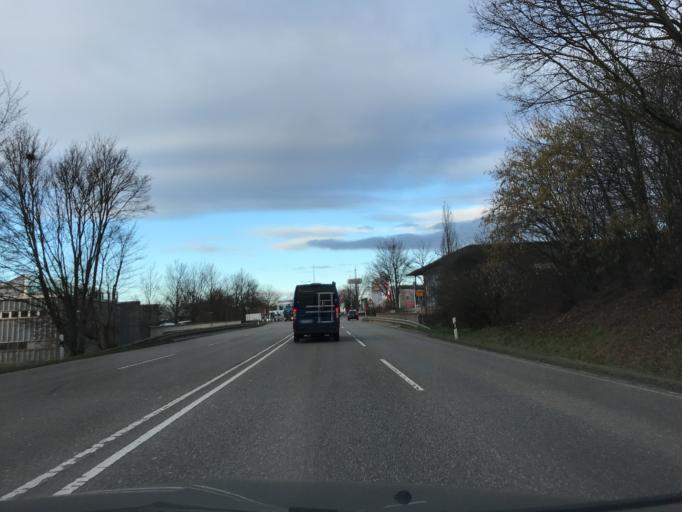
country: DE
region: Baden-Wuerttemberg
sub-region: Regierungsbezirk Stuttgart
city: Waiblingen
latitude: 48.8213
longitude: 9.3022
